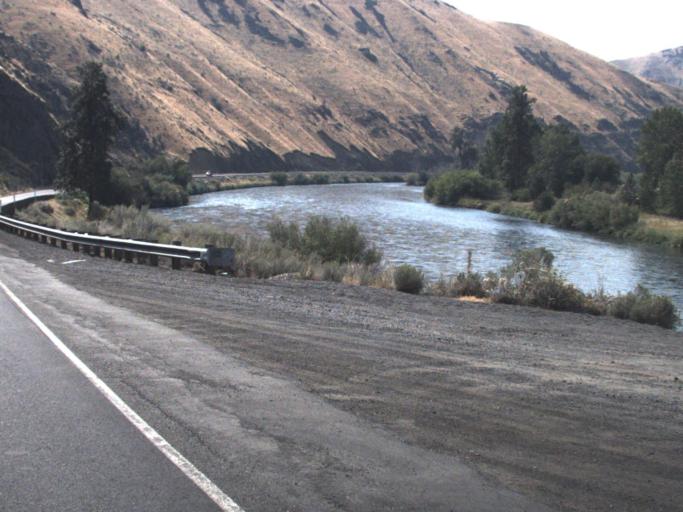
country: US
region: Washington
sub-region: Yakima County
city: Selah
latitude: 46.8027
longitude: -120.4420
